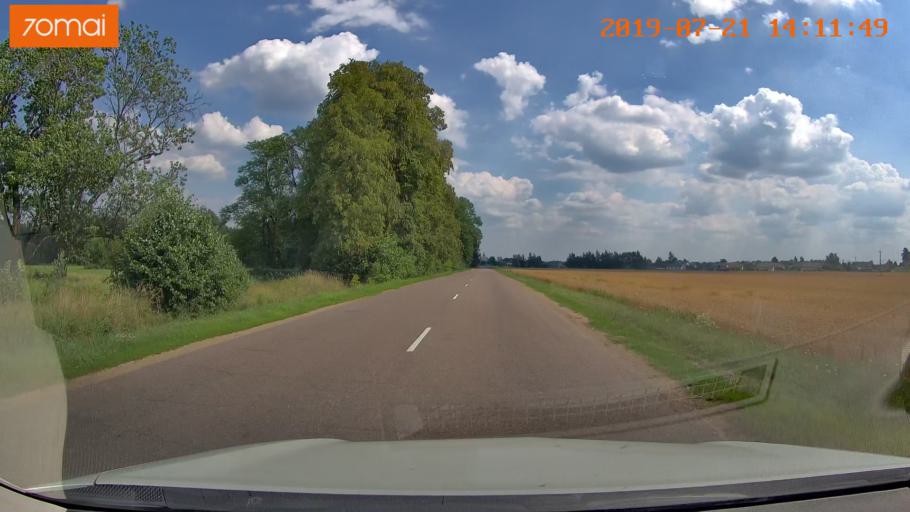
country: BY
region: Grodnenskaya
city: Karelichy
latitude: 53.6552
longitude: 26.1598
